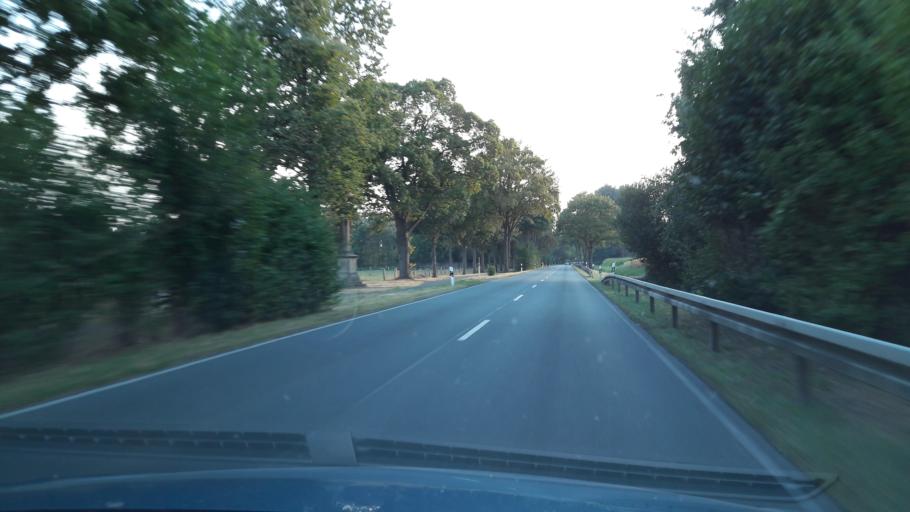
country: DE
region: North Rhine-Westphalia
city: Ahlen
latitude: 51.8142
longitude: 7.9499
